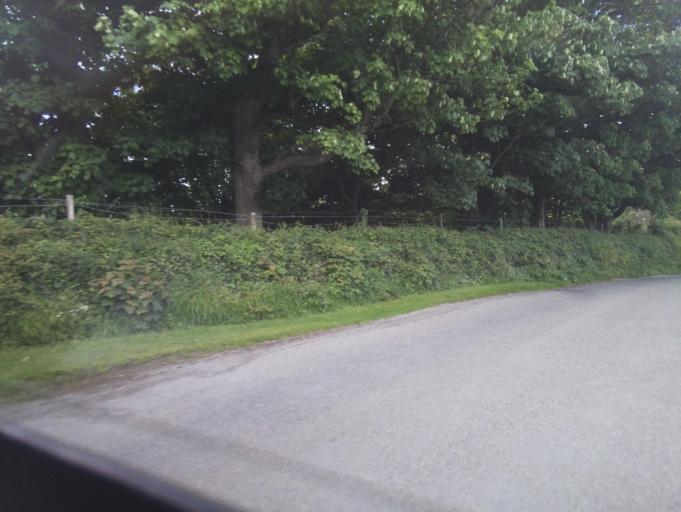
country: GB
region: England
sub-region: Devon
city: Dartmouth
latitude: 50.3593
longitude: -3.5471
